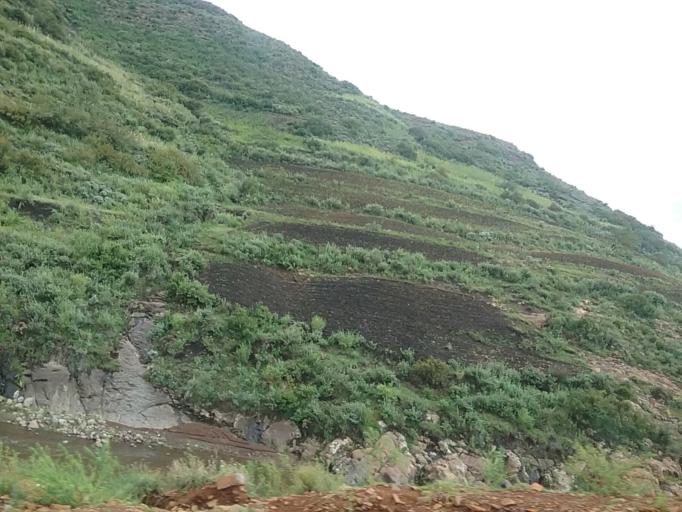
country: LS
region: Berea
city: Teyateyaneng
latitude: -29.2416
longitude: 27.9706
